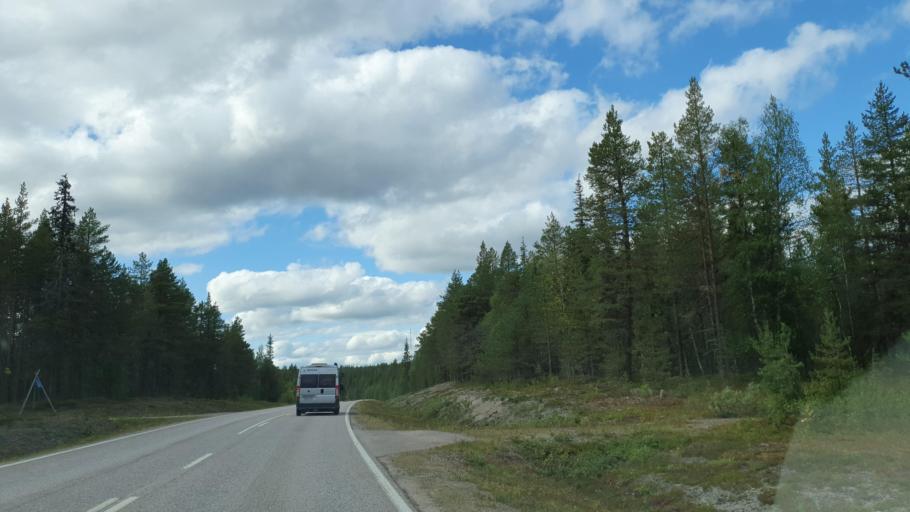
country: FI
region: Lapland
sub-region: Tunturi-Lappi
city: Muonio
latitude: 67.8602
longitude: 24.1347
